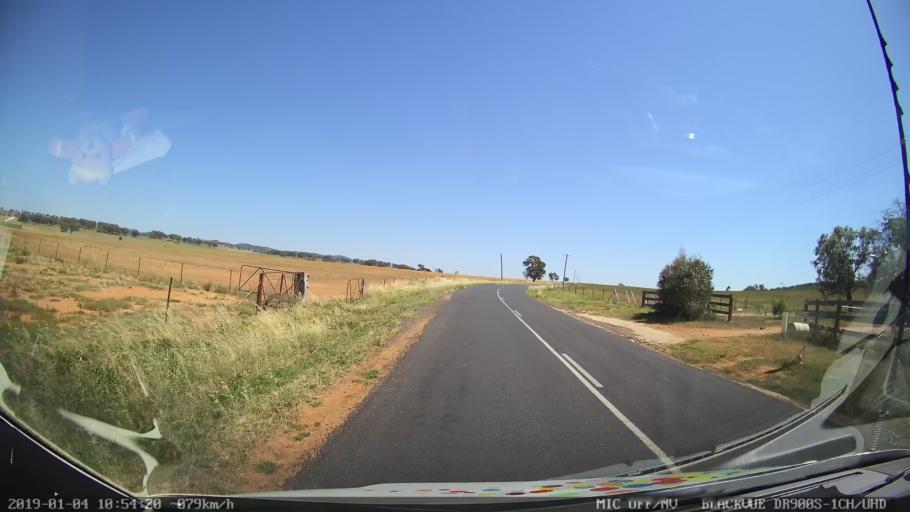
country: AU
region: New South Wales
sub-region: Cabonne
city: Molong
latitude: -33.2101
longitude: 148.6912
